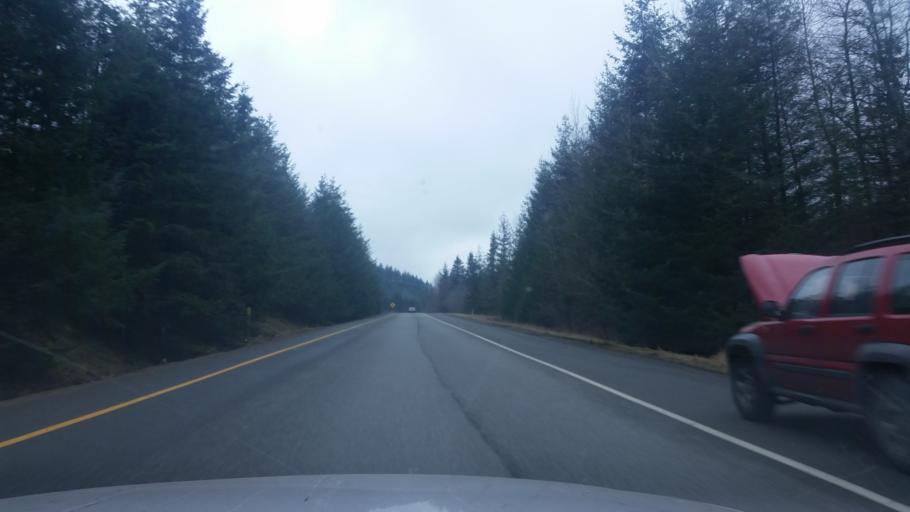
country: US
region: Washington
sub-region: King County
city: Snoqualmie
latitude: 47.5138
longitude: -121.8493
